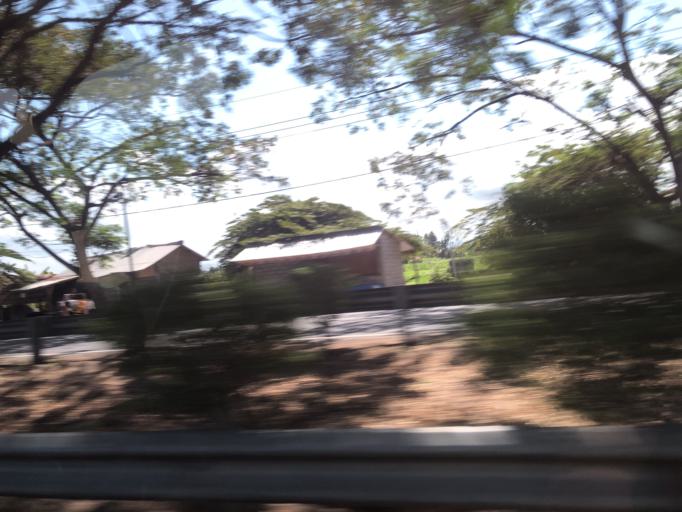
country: ID
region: Bali
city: Semarapura
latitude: -8.5668
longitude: 115.4133
